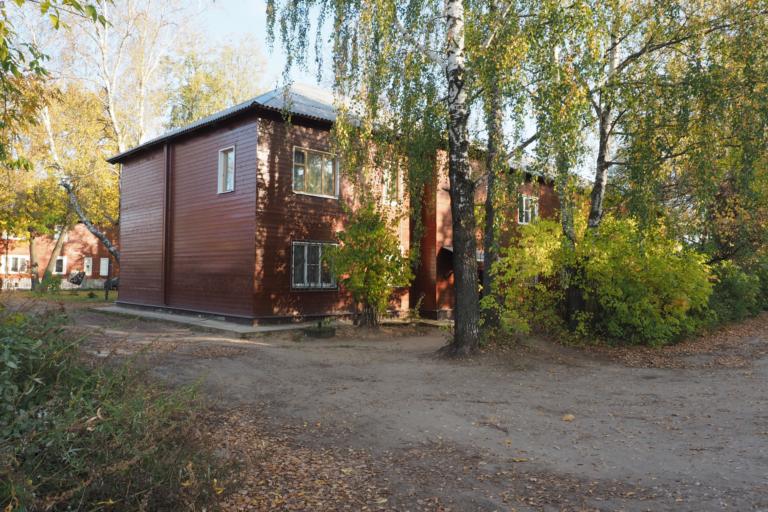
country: RU
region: Moskovskaya
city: Kurovskoye
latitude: 55.5765
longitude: 38.9042
